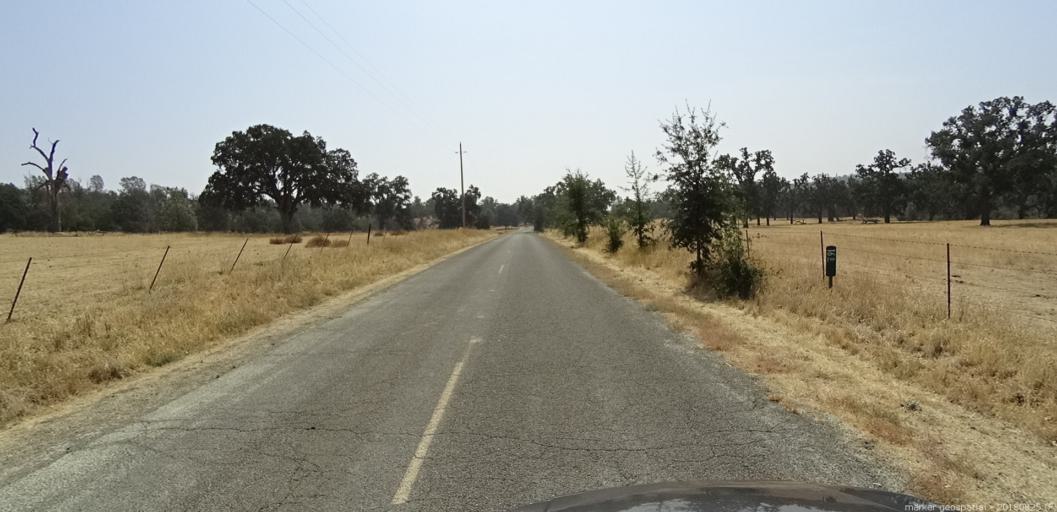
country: US
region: California
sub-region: Fresno County
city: Coalinga
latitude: 35.9204
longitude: -120.4918
